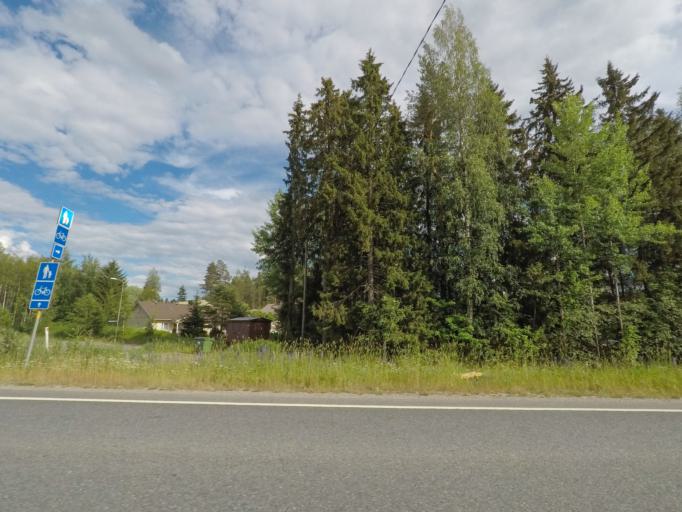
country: FI
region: Paijanne Tavastia
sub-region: Lahti
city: Lahti
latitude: 60.9398
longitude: 25.5970
